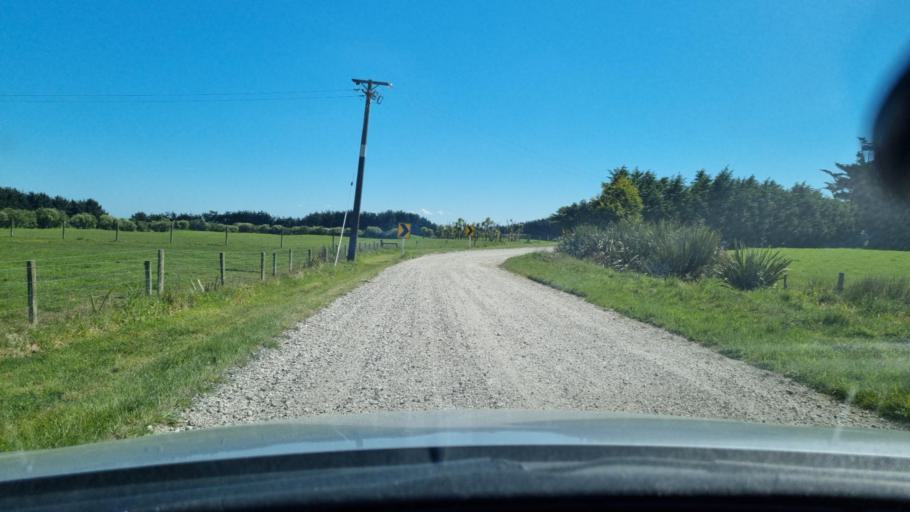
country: NZ
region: Southland
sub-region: Invercargill City
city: Invercargill
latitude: -46.4157
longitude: 168.2642
